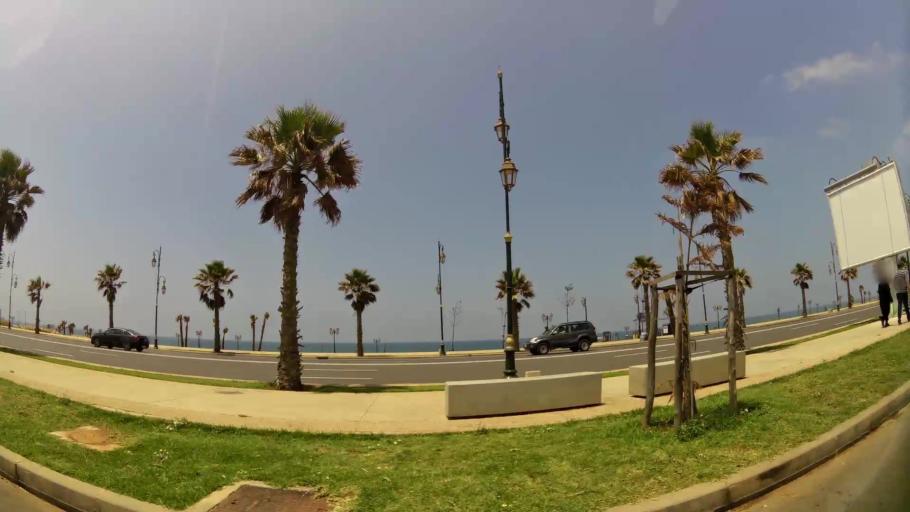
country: MA
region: Rabat-Sale-Zemmour-Zaer
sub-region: Skhirate-Temara
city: Temara
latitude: 33.9734
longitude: -6.9016
